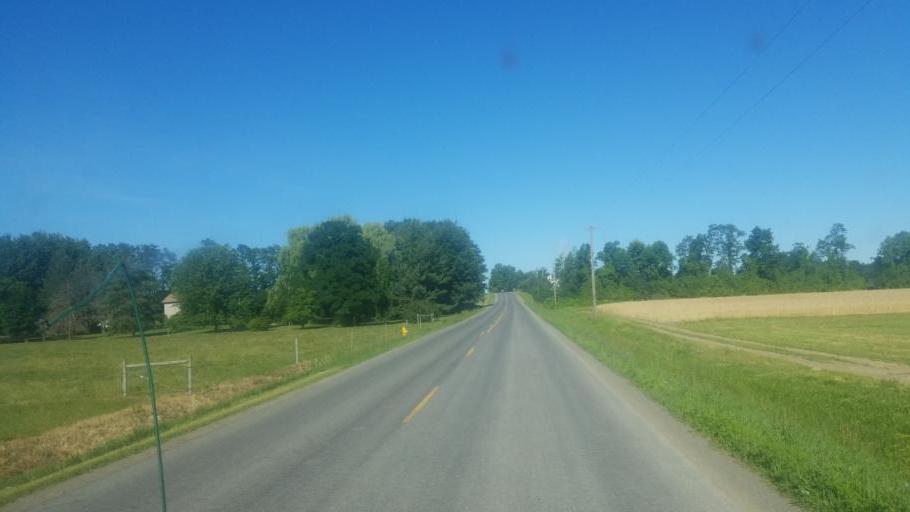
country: US
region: New York
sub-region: Ontario County
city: Canandaigua
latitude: 42.8373
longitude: -77.1752
